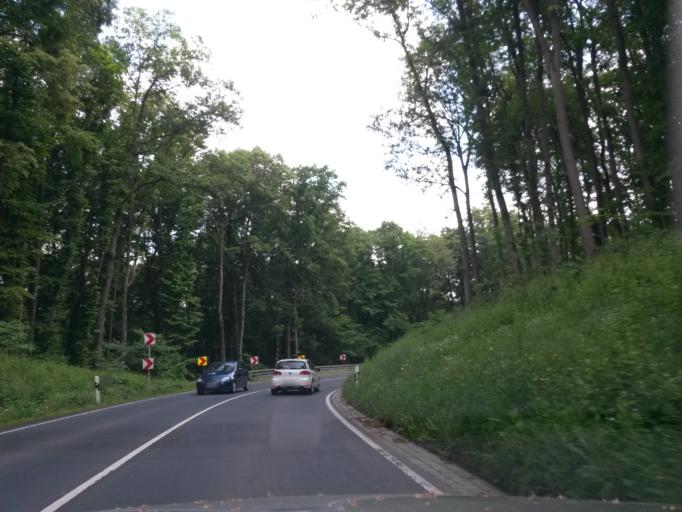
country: DE
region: Bavaria
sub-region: Regierungsbezirk Unterfranken
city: Nudlingen
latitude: 50.2163
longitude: 10.1078
